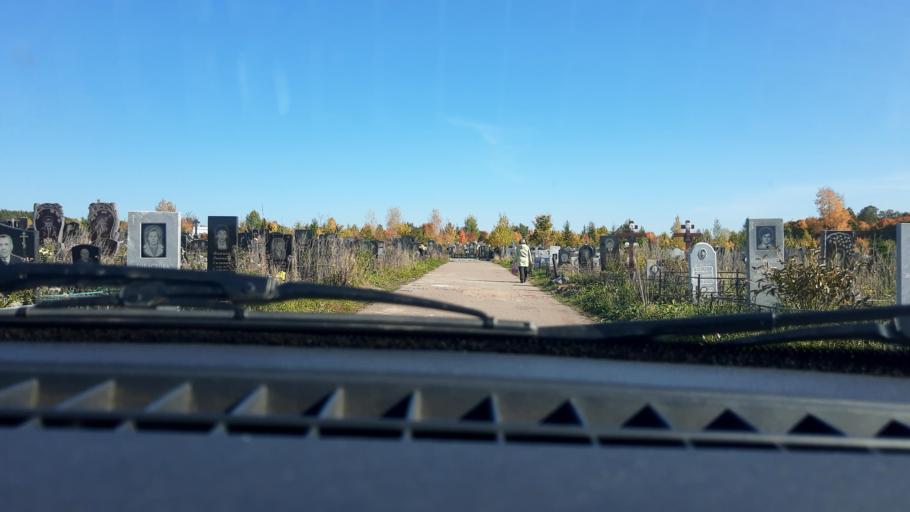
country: RU
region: Bashkortostan
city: Mikhaylovka
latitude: 54.8150
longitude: 55.8603
